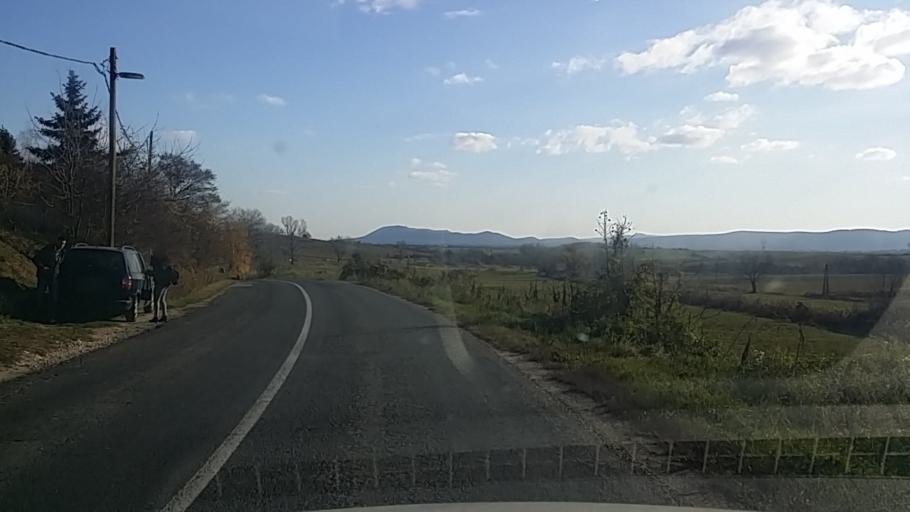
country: HU
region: Pest
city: Pilisszanto
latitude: 47.6607
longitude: 18.8954
